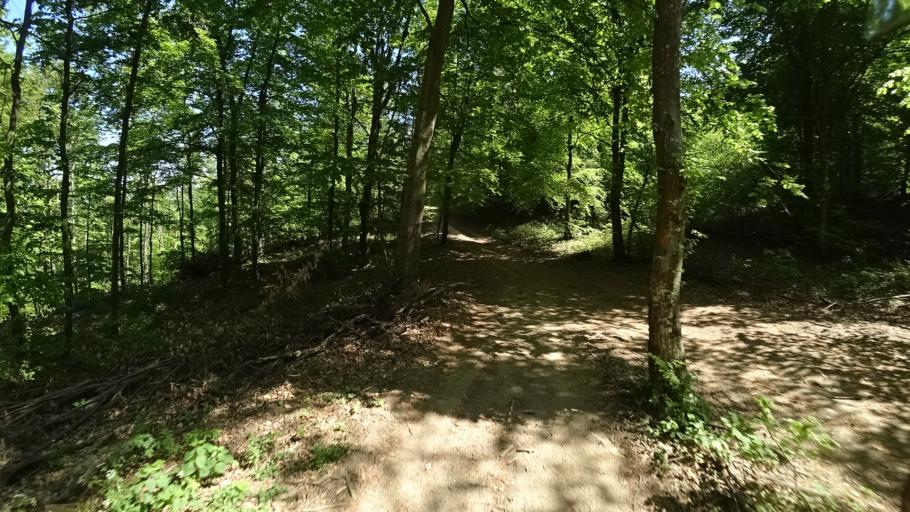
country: HR
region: Zagrebacka
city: Jablanovec
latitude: 45.8684
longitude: 15.8617
